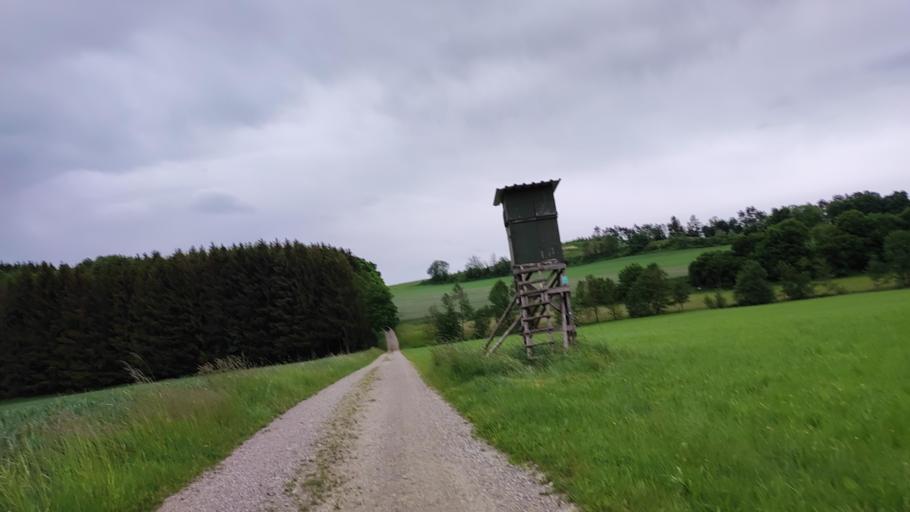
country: DE
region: Bavaria
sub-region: Swabia
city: Dinkelscherben
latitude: 48.3538
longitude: 10.5468
